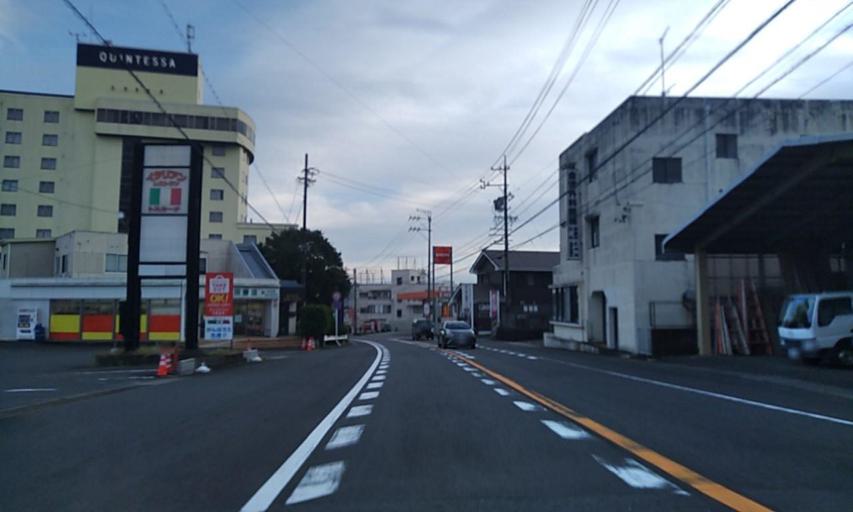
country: JP
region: Mie
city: Toba
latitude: 34.3329
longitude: 136.8182
